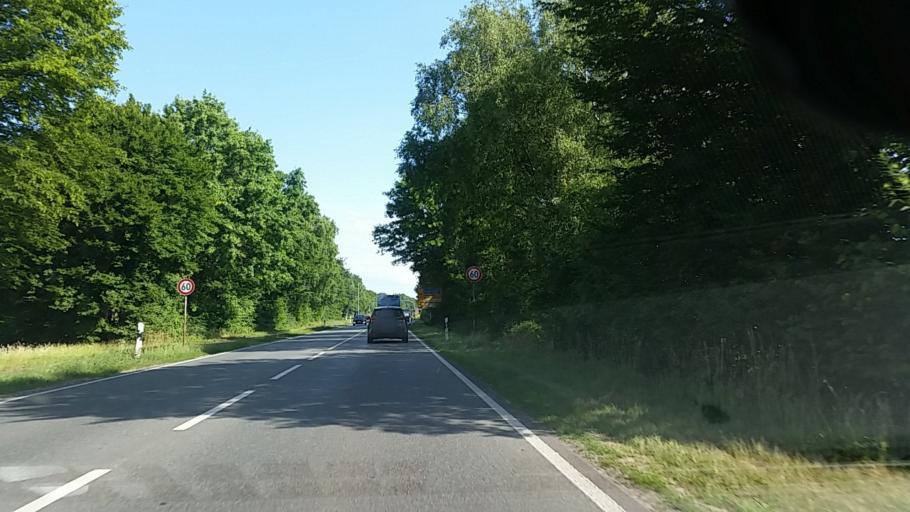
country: DE
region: Schleswig-Holstein
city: Tangstedt
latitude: 53.7209
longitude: 10.0274
